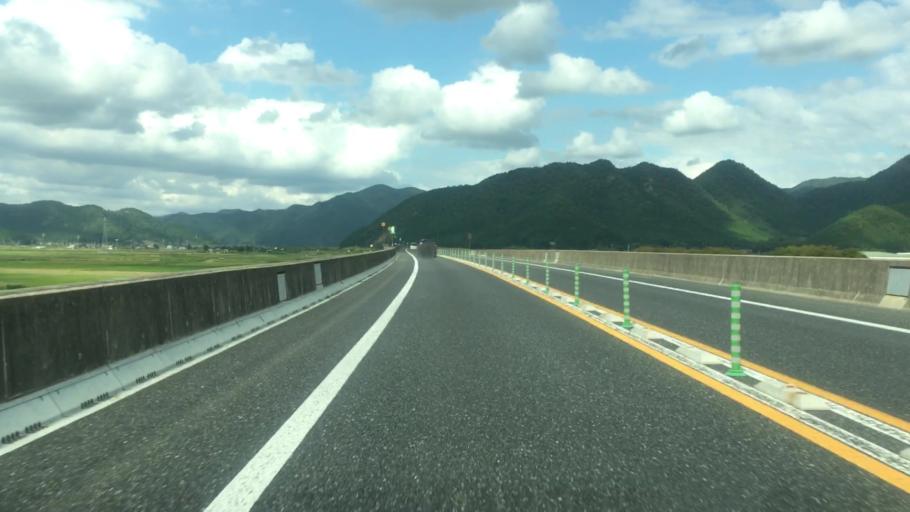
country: JP
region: Kyoto
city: Fukuchiyama
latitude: 35.1954
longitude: 135.0427
